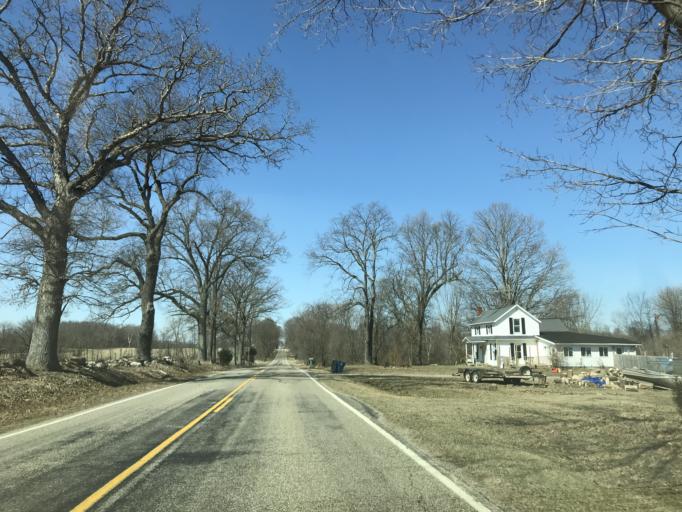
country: US
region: Michigan
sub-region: Hillsdale County
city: Litchfield
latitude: 41.9856
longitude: -84.7602
